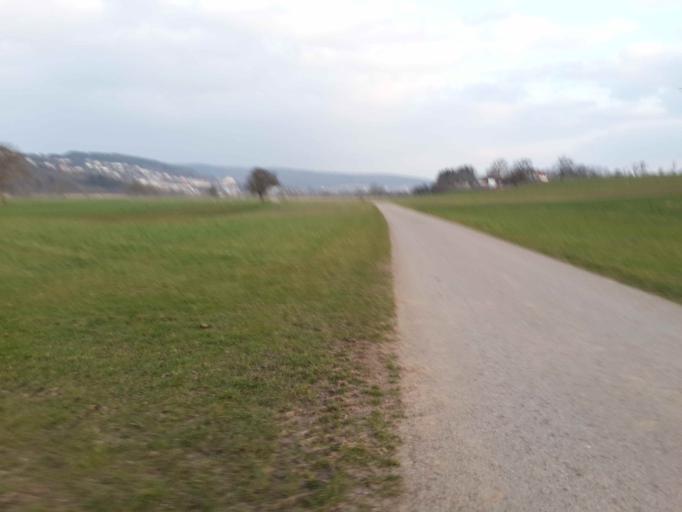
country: DE
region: Baden-Wuerttemberg
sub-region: Karlsruhe Region
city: Obrigheim
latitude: 49.3633
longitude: 9.0919
